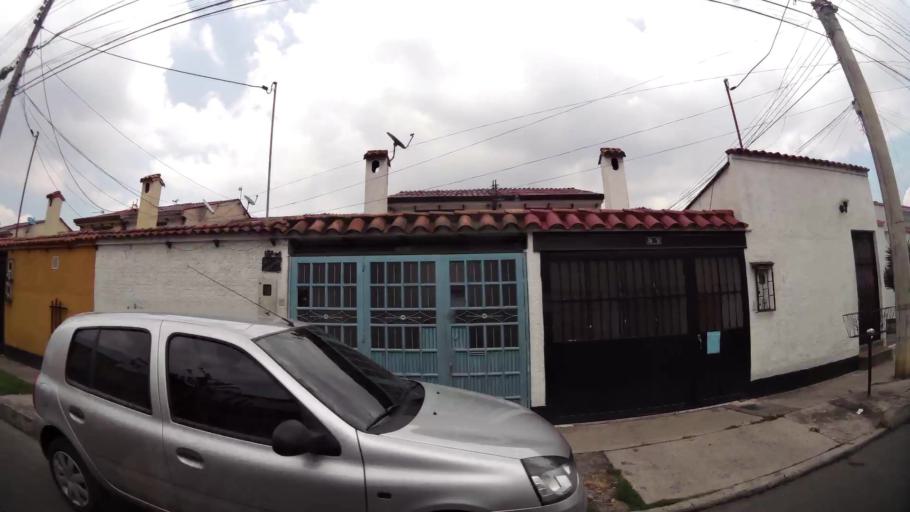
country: CO
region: Cundinamarca
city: Cota
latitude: 4.7531
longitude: -74.0485
